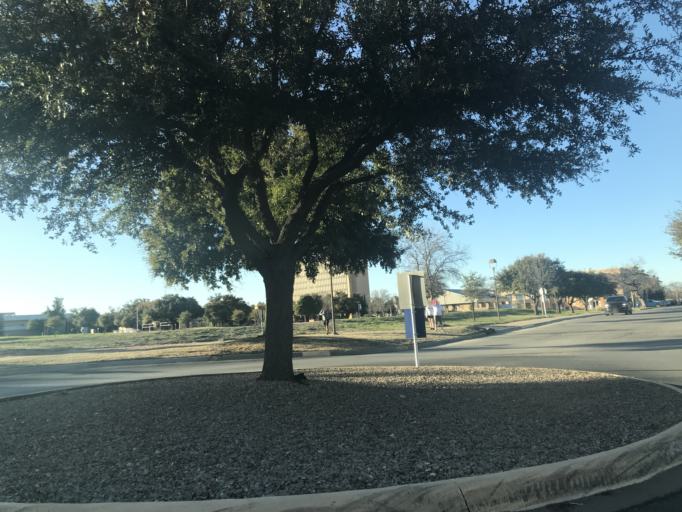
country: US
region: Texas
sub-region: Tom Green County
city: San Angelo
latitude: 31.4389
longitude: -100.4573
